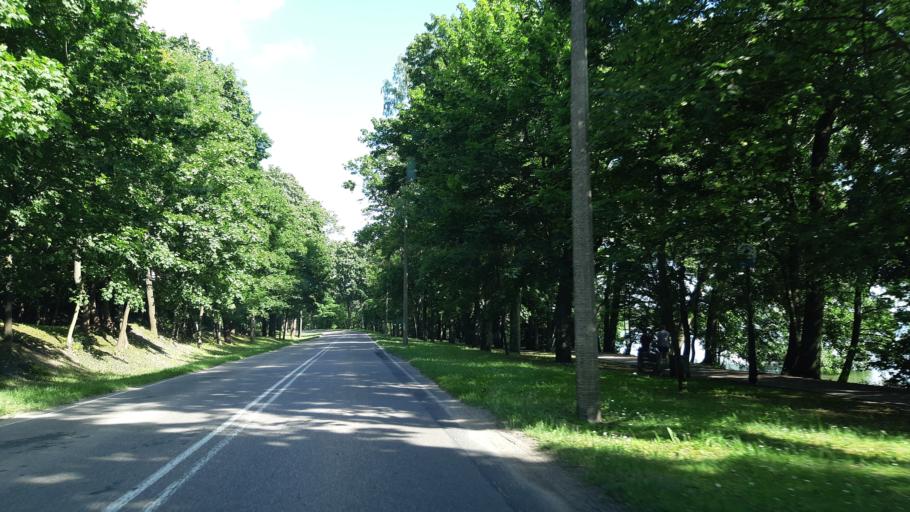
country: PL
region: Warmian-Masurian Voivodeship
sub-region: Powiat mragowski
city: Mragowo
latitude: 53.8771
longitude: 21.3095
